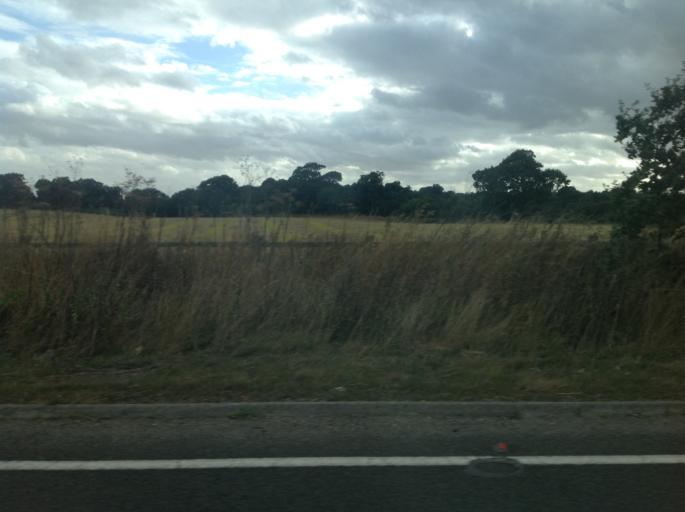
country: GB
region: England
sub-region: Suffolk
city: Kesgrave
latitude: 52.0226
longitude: 1.2602
